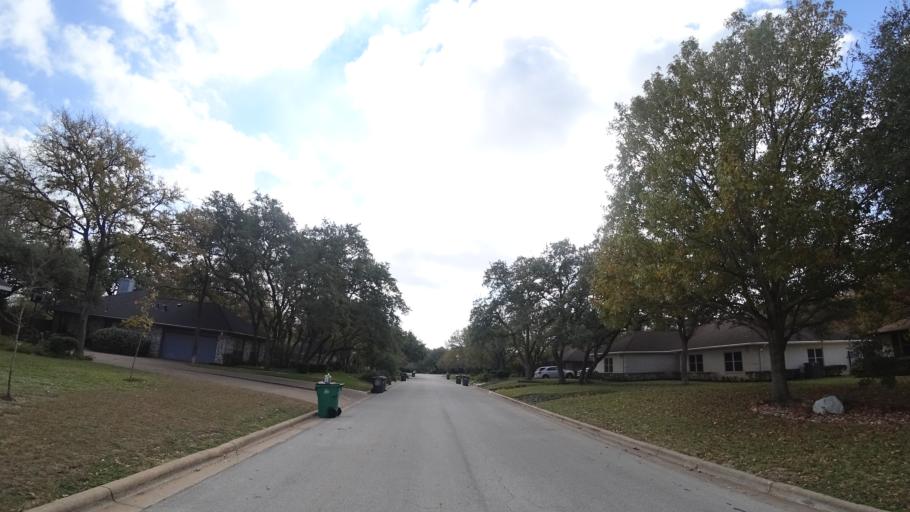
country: US
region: Texas
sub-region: Travis County
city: Shady Hollow
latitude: 30.1718
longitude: -97.8510
